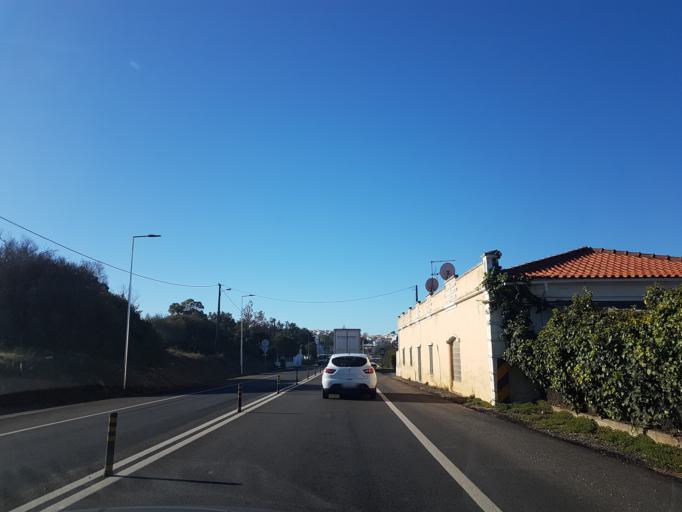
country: PT
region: Faro
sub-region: Silves
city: Armacao de Pera
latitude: 37.1312
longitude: -8.3946
